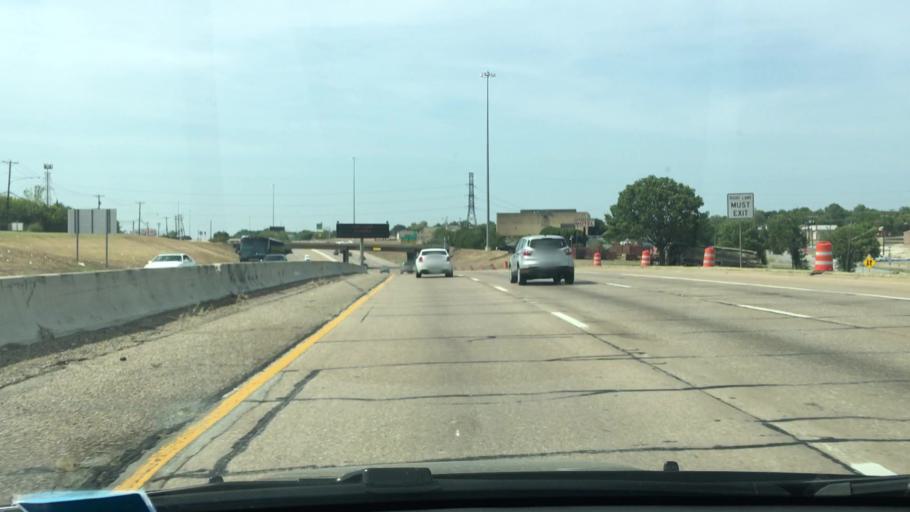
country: US
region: Texas
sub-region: Dallas County
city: Cockrell Hill
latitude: 32.6988
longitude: -96.8236
